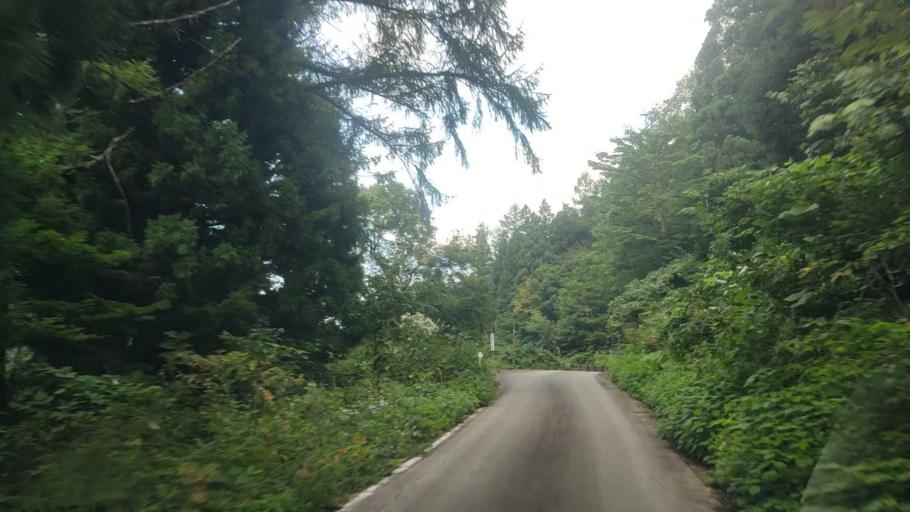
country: JP
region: Toyama
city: Yatsuomachi-higashikumisaka
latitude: 36.4148
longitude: 137.0807
